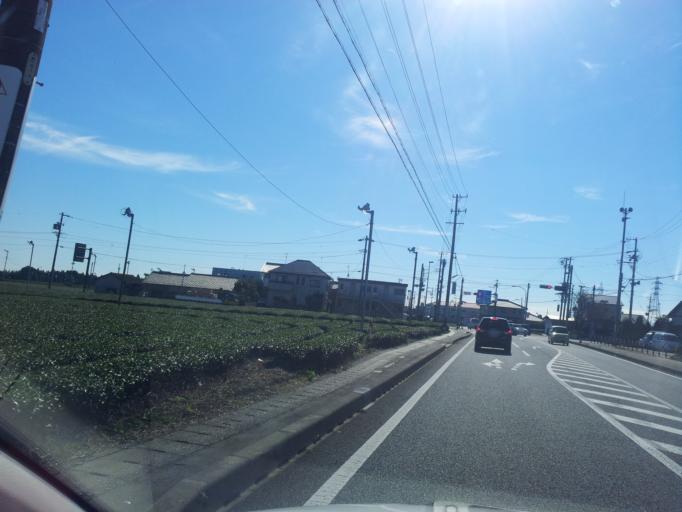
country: JP
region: Shizuoka
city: Kanaya
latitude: 34.8052
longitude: 138.1352
